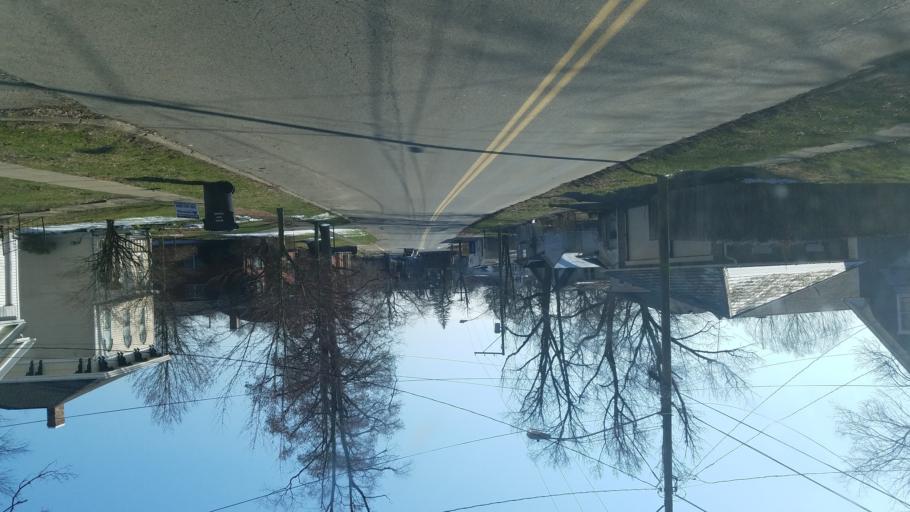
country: US
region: Ohio
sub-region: Knox County
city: Mount Vernon
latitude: 40.4015
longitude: -82.4855
